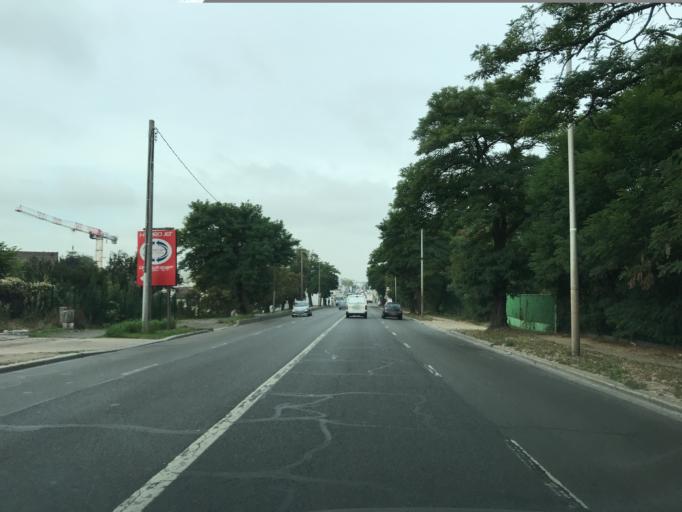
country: FR
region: Ile-de-France
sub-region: Departement de Seine-Saint-Denis
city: Drancy
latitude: 48.9098
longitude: 2.4304
